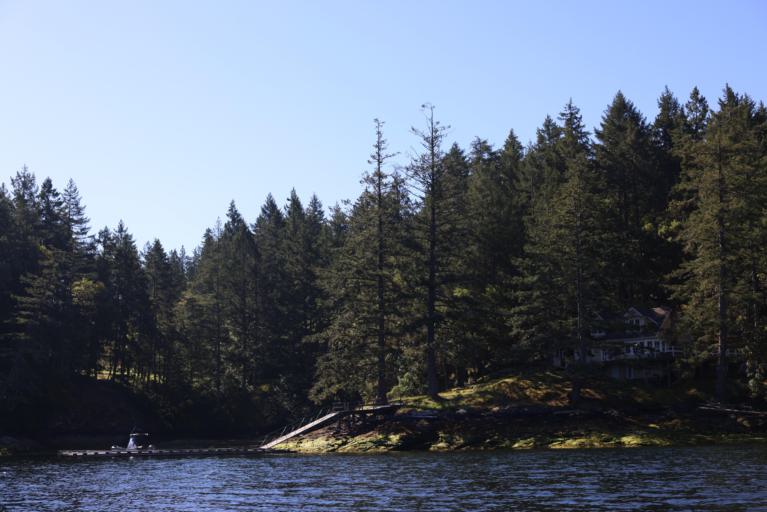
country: CA
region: British Columbia
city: North Cowichan
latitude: 48.8066
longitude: -123.5906
